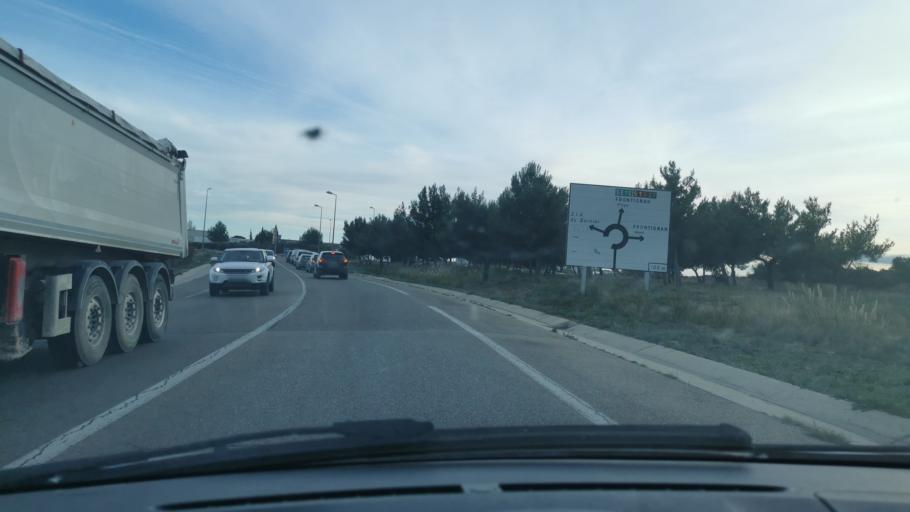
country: FR
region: Languedoc-Roussillon
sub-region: Departement de l'Herault
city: Frontignan
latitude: 43.4674
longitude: 3.7661
